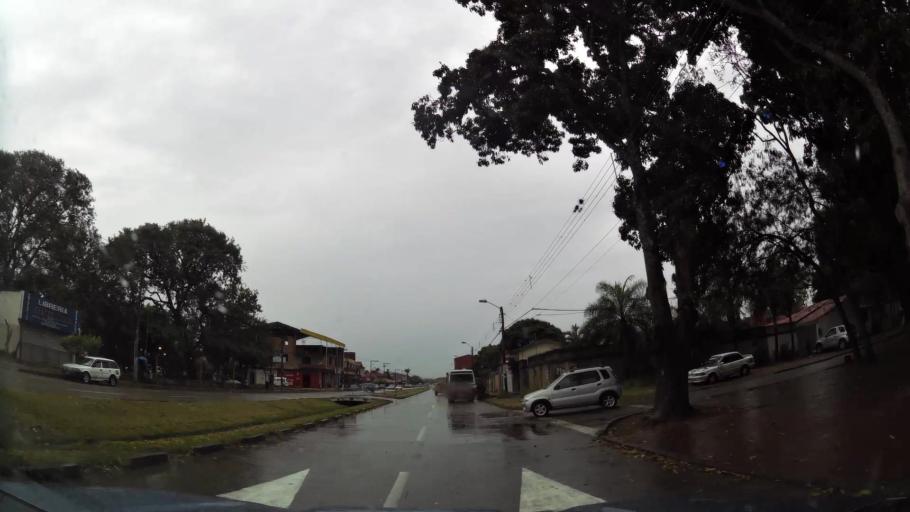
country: BO
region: Santa Cruz
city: Santa Cruz de la Sierra
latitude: -17.7911
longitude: -63.2114
